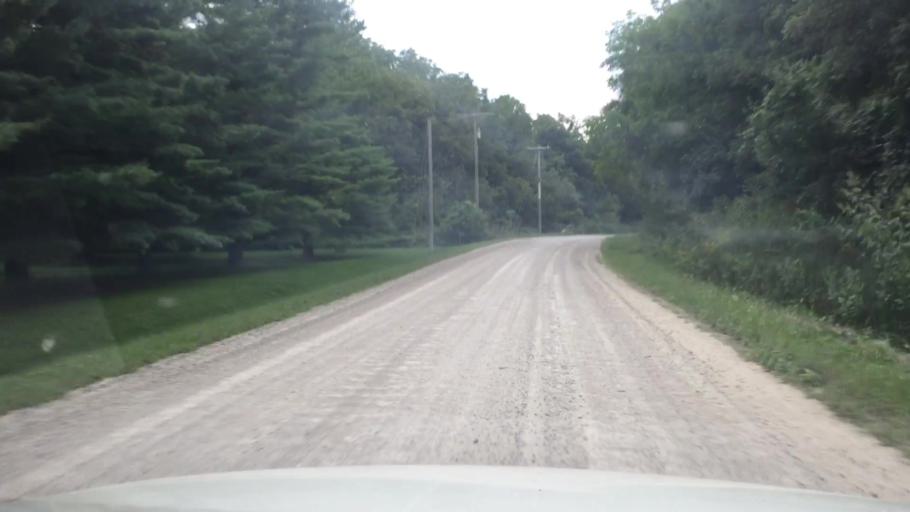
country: US
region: Iowa
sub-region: Story County
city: Huxley
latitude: 41.9074
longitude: -93.5758
